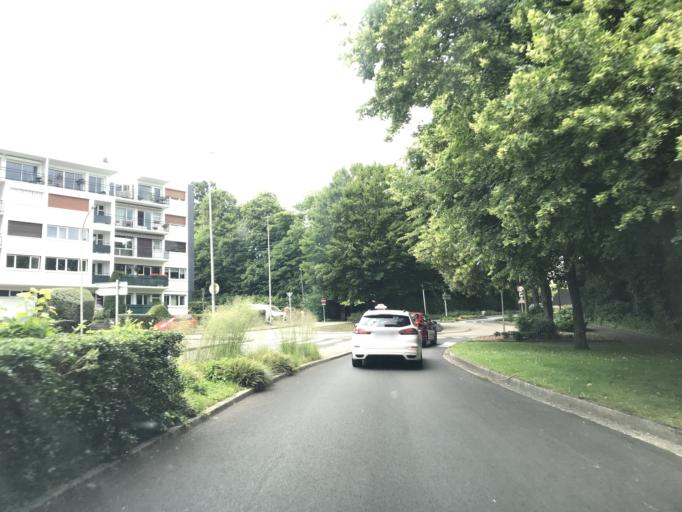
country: FR
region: Haute-Normandie
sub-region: Departement de la Seine-Maritime
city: Mont-Saint-Aignan
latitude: 49.4648
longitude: 1.0871
